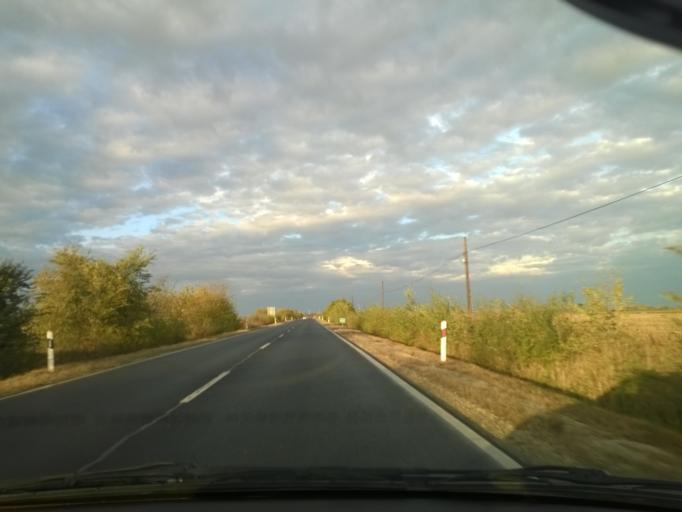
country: HU
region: Bacs-Kiskun
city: Dunapataj
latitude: 46.6196
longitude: 18.9924
